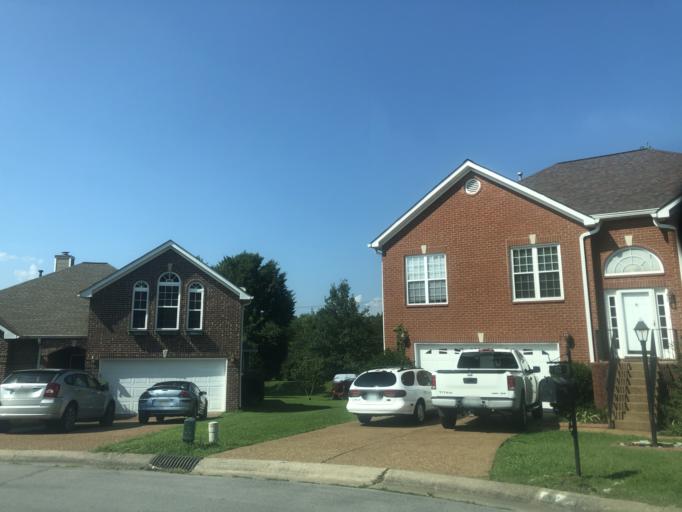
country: US
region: Tennessee
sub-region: Wilson County
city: Green Hill
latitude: 36.1510
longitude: -86.5846
